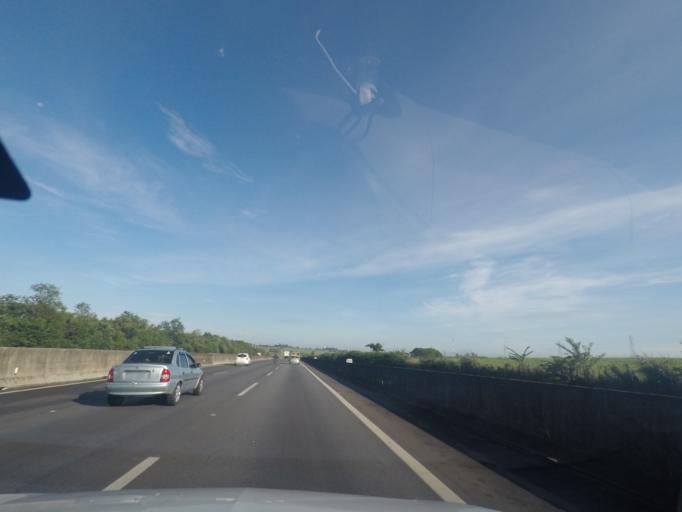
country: BR
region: Sao Paulo
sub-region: Nova Odessa
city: Nova Odessa
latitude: -22.7462
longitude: -47.2656
